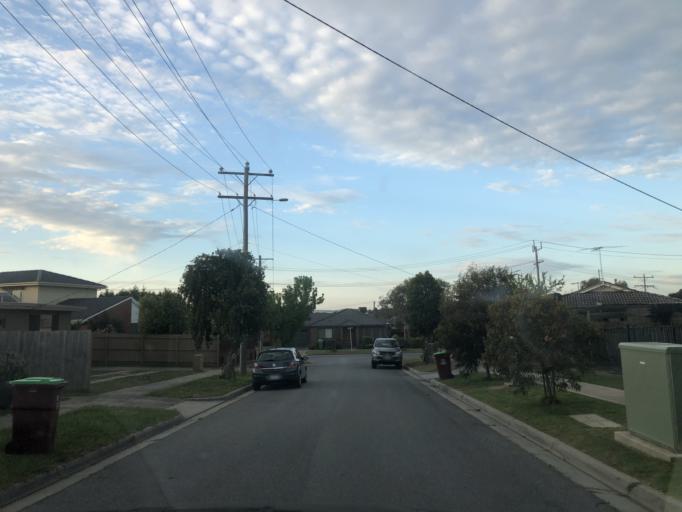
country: AU
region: Victoria
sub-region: Casey
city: Hampton Park
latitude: -38.0311
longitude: 145.2613
